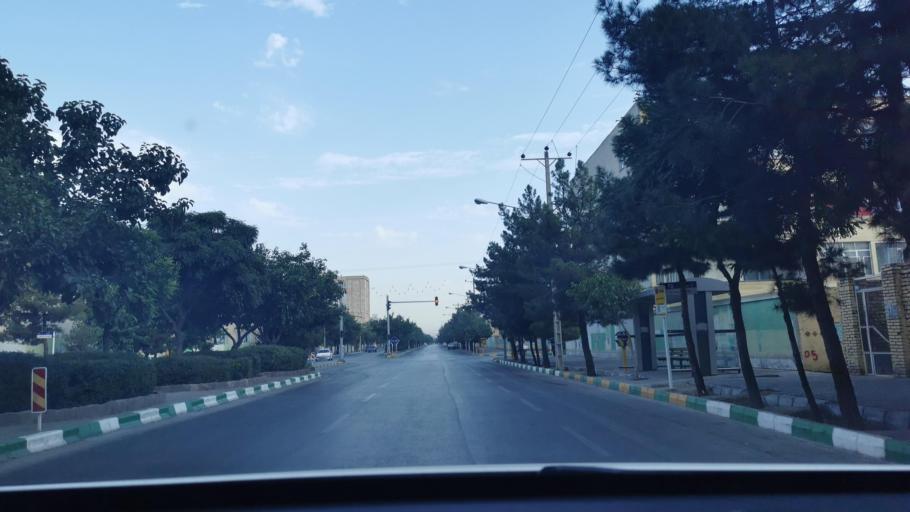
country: IR
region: Razavi Khorasan
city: Mashhad
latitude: 36.3576
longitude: 59.5252
